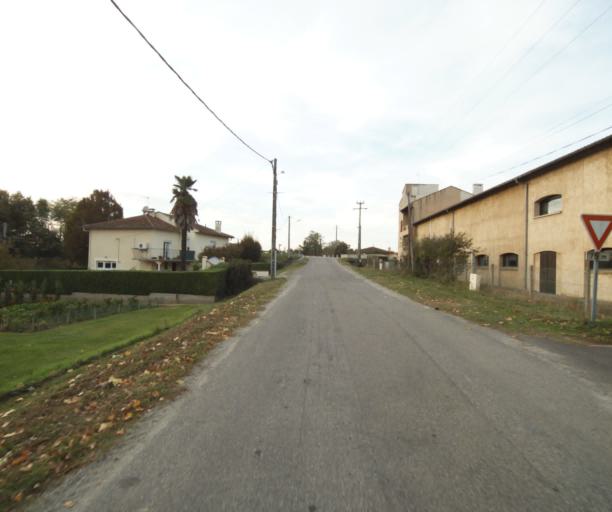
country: FR
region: Midi-Pyrenees
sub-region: Departement du Tarn-et-Garonne
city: Grisolles
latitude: 43.8282
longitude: 1.3023
